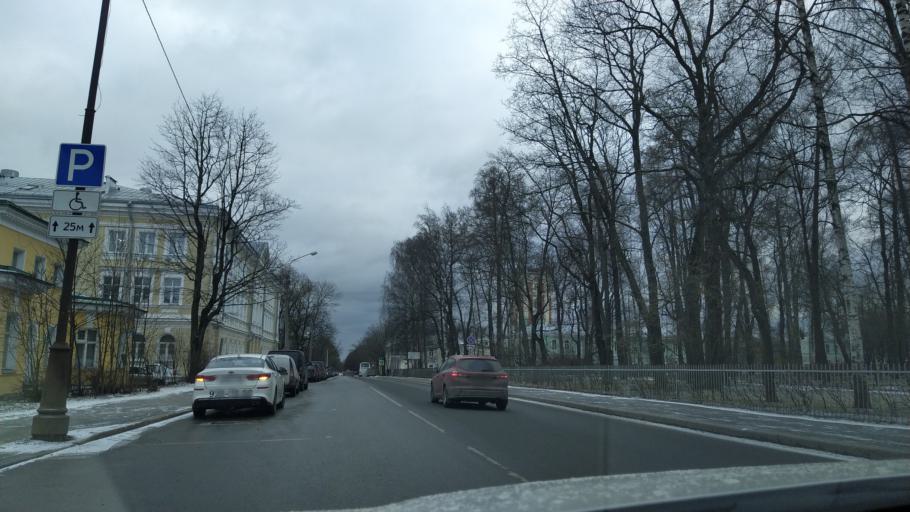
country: RU
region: St.-Petersburg
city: Pushkin
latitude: 59.7193
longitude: 30.3966
